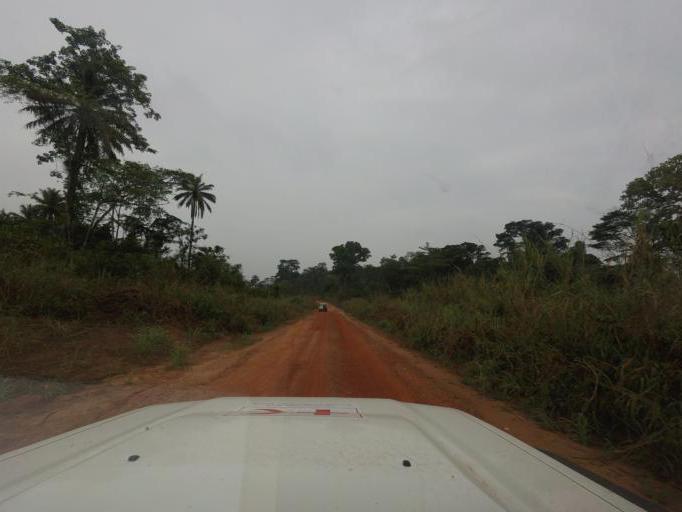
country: LR
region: Lofa
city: Voinjama
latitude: 8.3927
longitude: -9.8082
